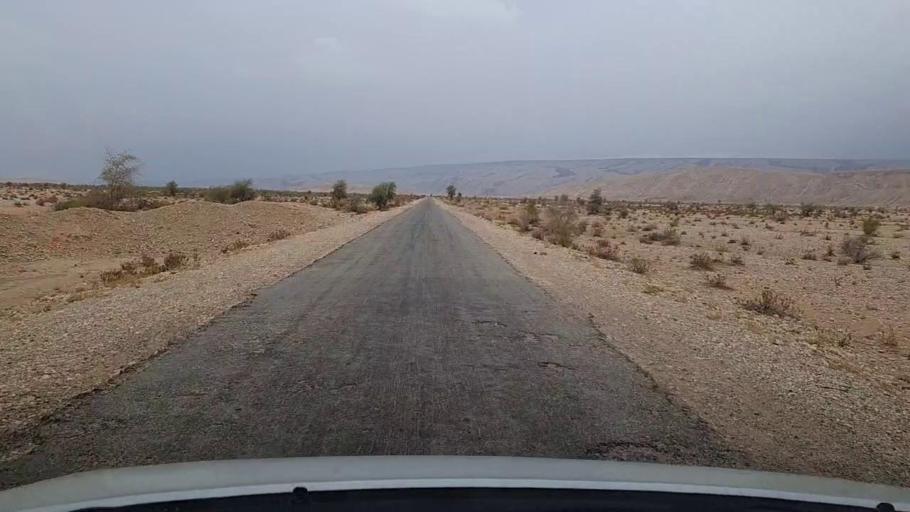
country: PK
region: Sindh
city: Sehwan
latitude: 26.2563
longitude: 67.7211
